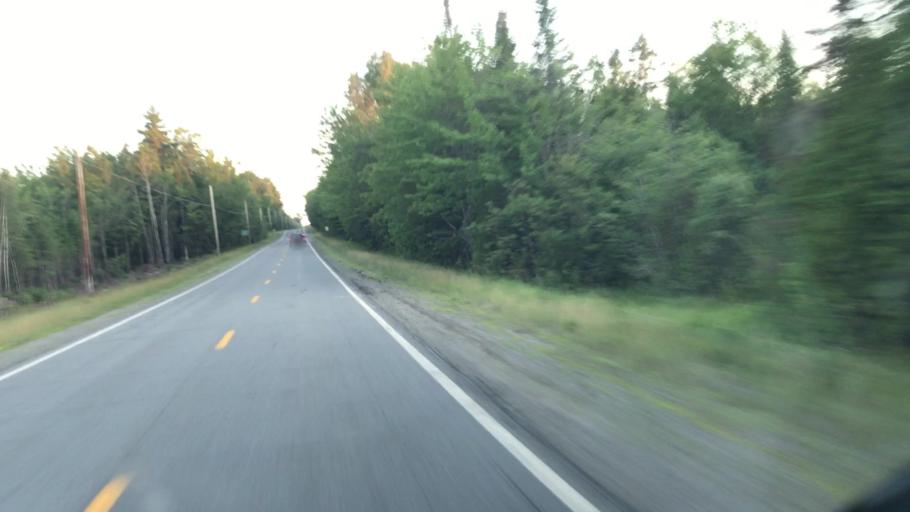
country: US
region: Maine
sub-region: Penobscot County
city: Medway
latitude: 45.5895
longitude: -68.3136
